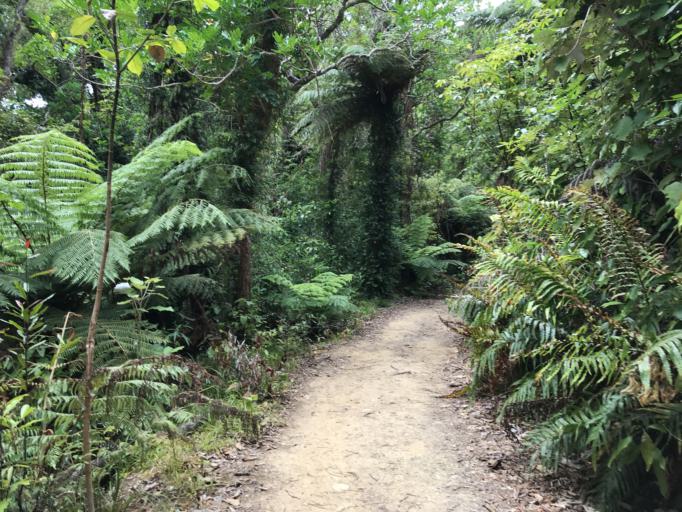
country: NZ
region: Marlborough
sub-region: Marlborough District
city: Picton
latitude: -41.0945
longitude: 174.1882
